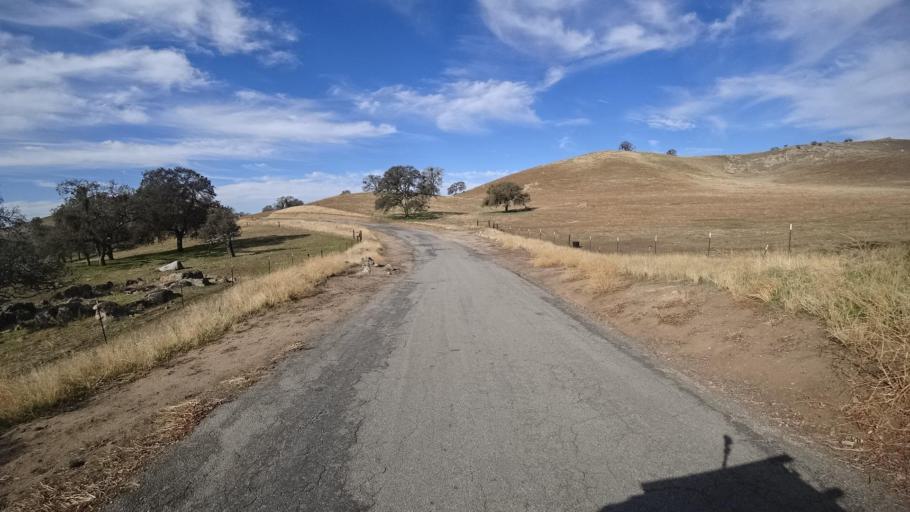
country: US
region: California
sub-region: Kern County
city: Oildale
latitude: 35.6082
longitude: -118.8278
